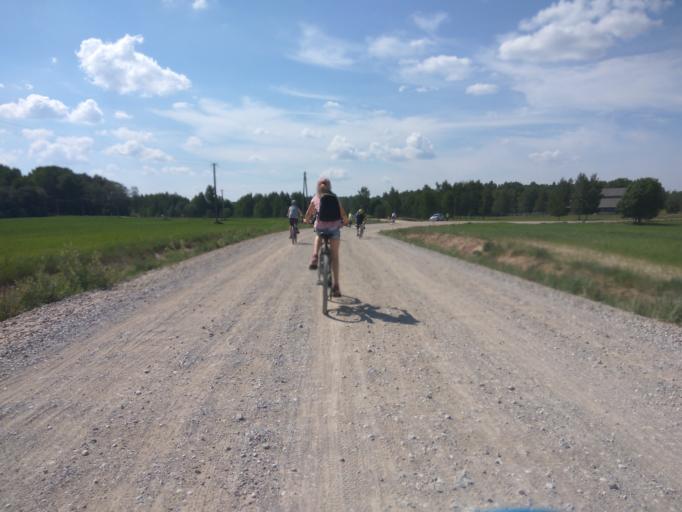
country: LV
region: Kuldigas Rajons
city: Kuldiga
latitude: 56.9404
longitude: 21.9728
